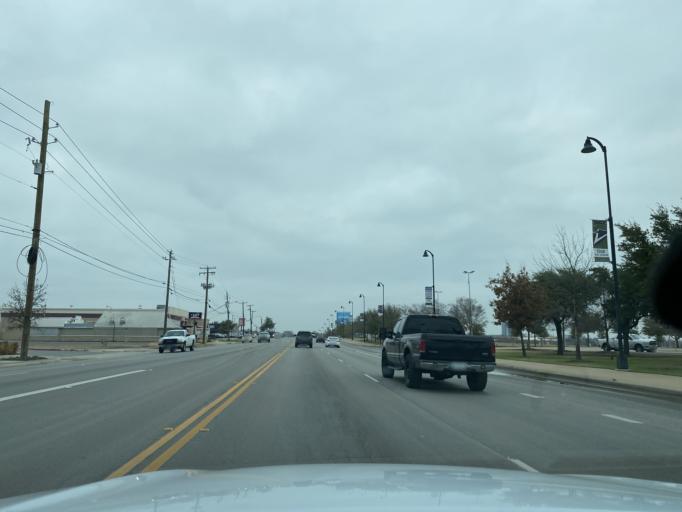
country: US
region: Texas
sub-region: Tarrant County
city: Arlington
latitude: 32.7462
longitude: -97.0973
